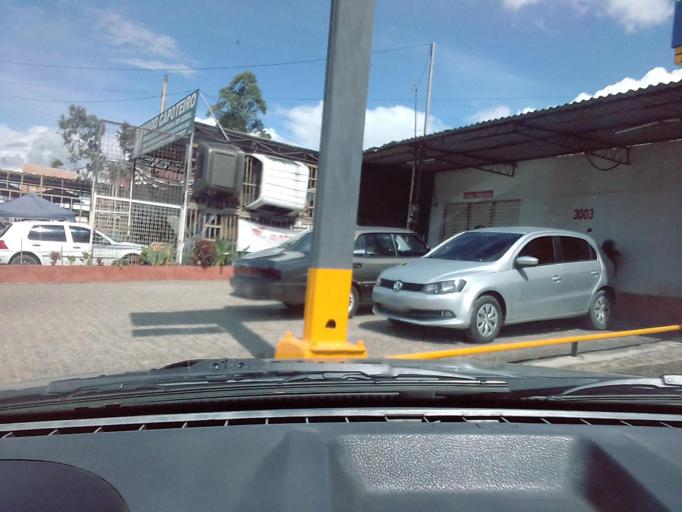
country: BR
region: Pernambuco
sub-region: Vitoria De Santo Antao
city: Vitoria de Santo Antao
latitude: -8.1177
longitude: -35.3048
